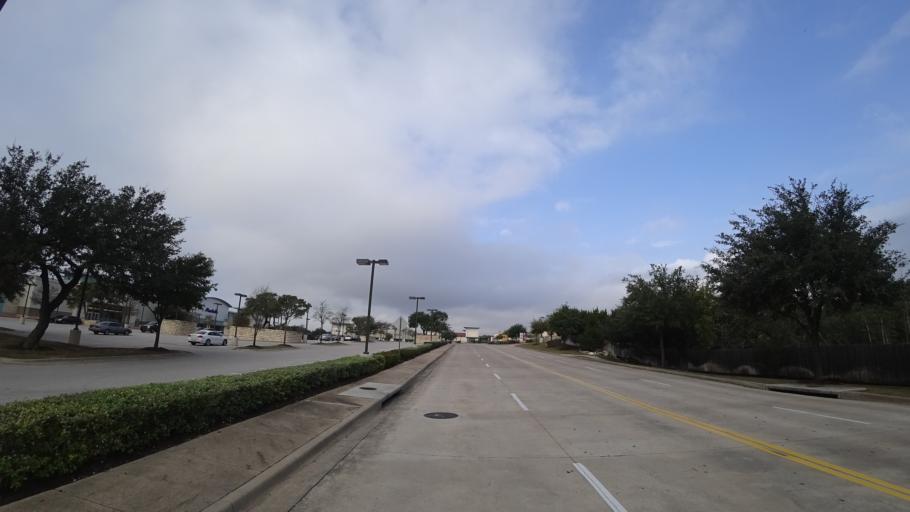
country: US
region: Texas
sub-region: Travis County
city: Bee Cave
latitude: 30.3061
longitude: -97.9434
